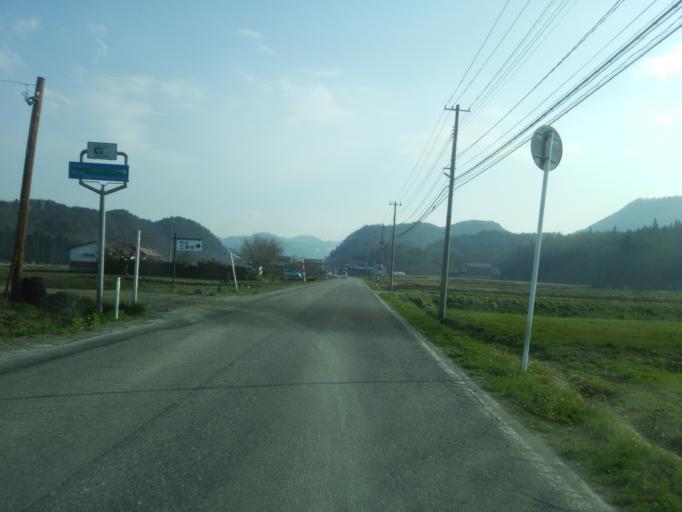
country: JP
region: Fukushima
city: Kitakata
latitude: 37.6826
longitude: 139.9011
